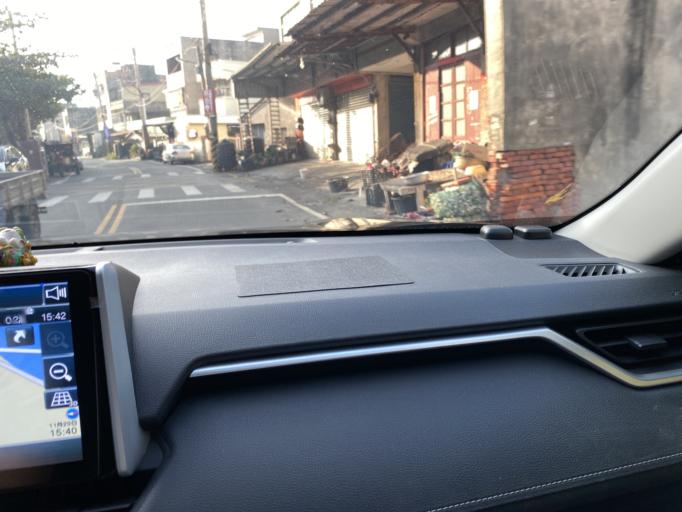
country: TW
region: Taiwan
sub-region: Changhua
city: Chang-hua
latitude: 23.9647
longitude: 120.3422
